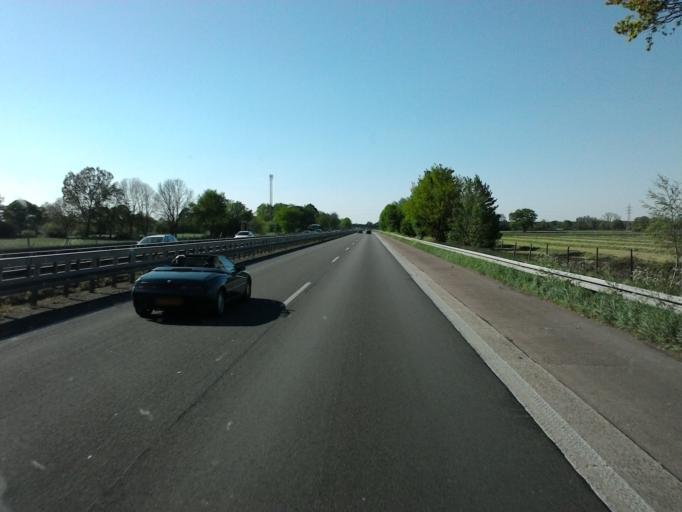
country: DE
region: North Rhine-Westphalia
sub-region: Regierungsbezirk Dusseldorf
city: Hamminkeln
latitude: 51.7604
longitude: 6.5551
